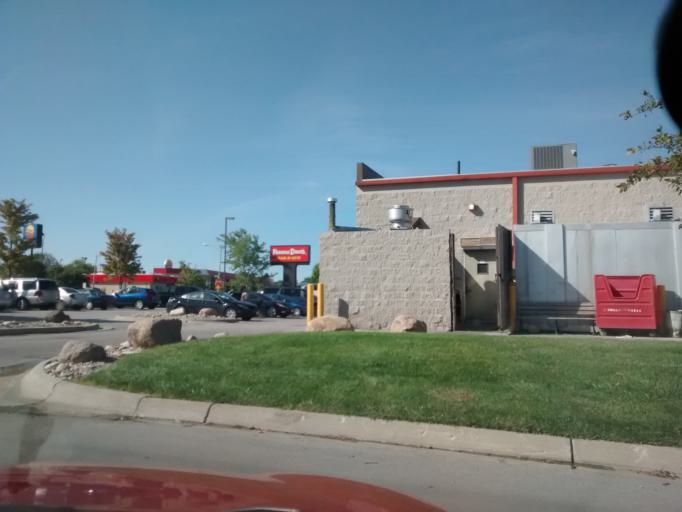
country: US
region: Nebraska
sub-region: Sarpy County
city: Offutt Air Force Base
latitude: 41.1574
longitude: -95.9420
